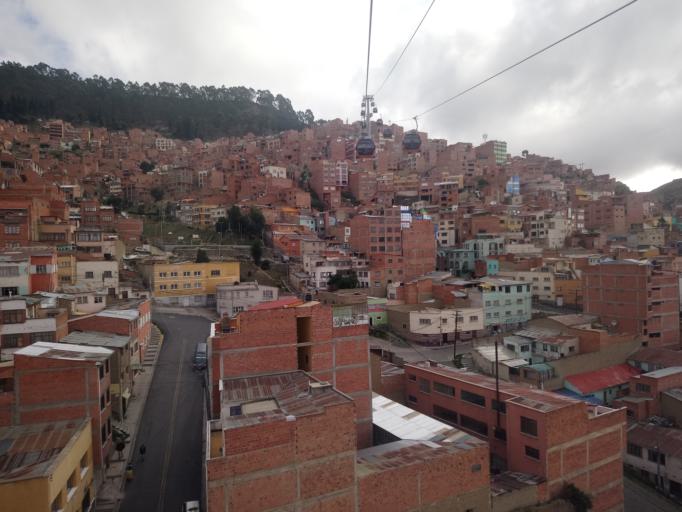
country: BO
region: La Paz
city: La Paz
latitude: -16.4892
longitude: -68.1352
